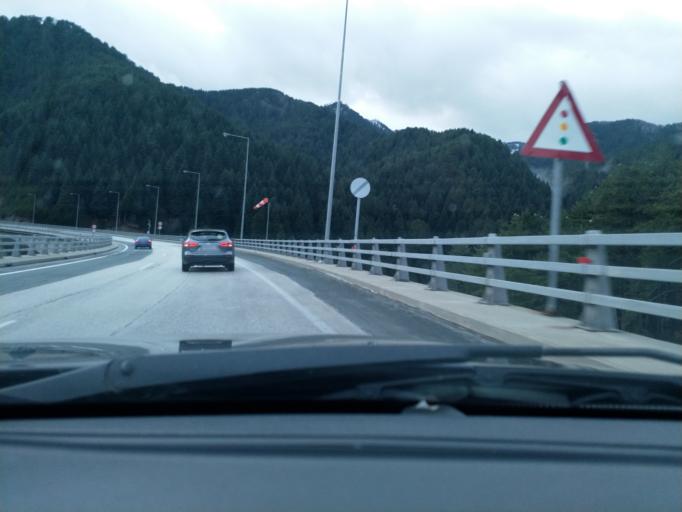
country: GR
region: Epirus
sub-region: Nomos Ioanninon
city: Metsovo
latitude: 39.7900
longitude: 21.2649
